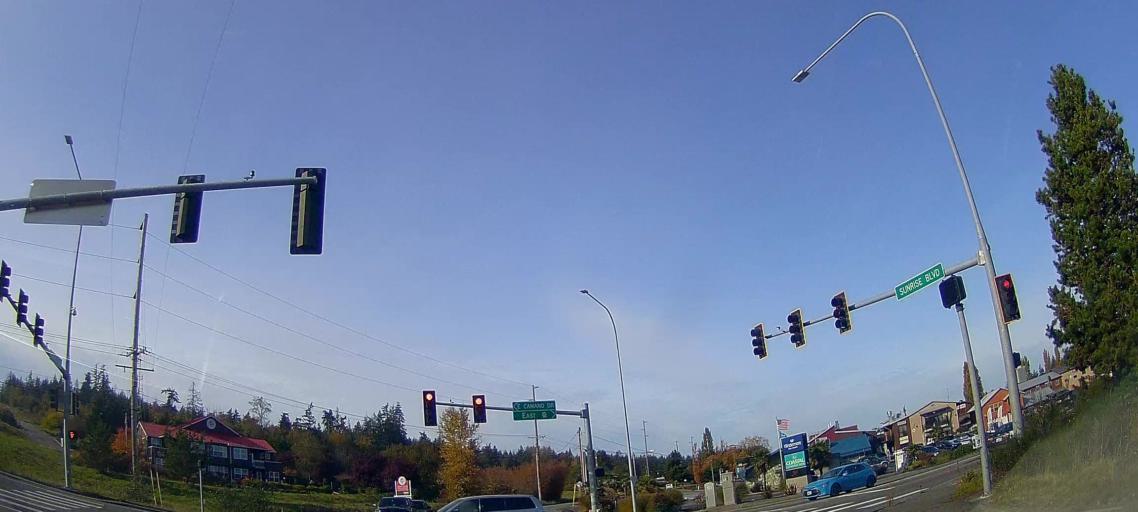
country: US
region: Washington
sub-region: Snohomish County
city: Stanwood
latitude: 48.2400
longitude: -122.4552
